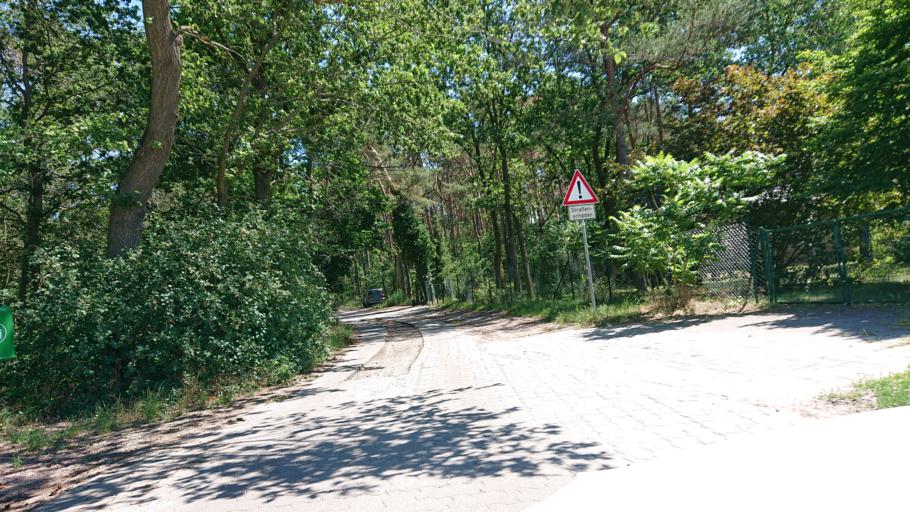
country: DE
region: Brandenburg
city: Potsdam
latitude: 52.3460
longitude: 13.1151
